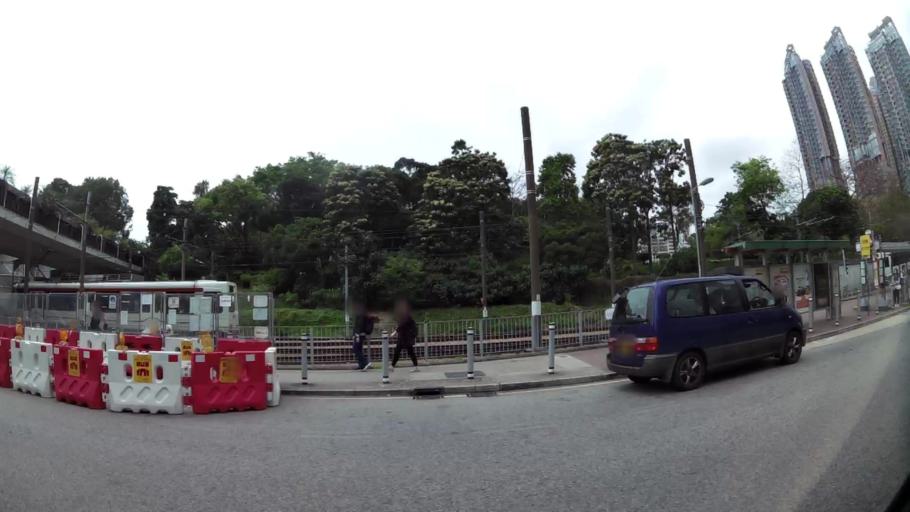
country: HK
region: Tuen Mun
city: Tuen Mun
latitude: 22.3920
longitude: 113.9751
